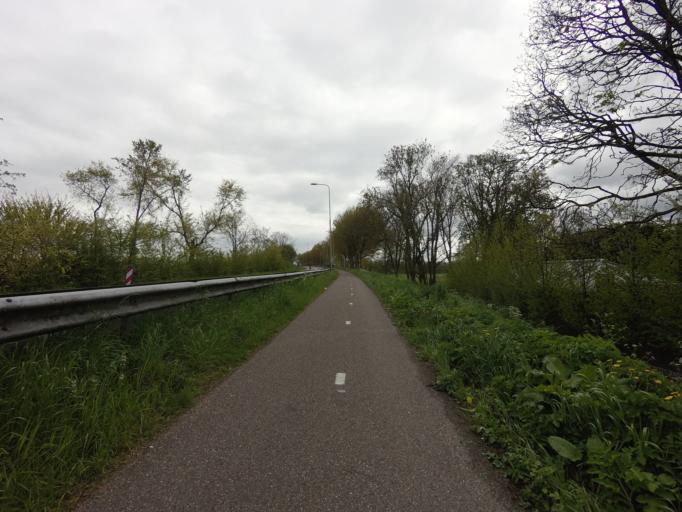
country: NL
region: North Holland
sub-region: Gemeente Amsterdam
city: Driemond
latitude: 52.3034
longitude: 5.0153
